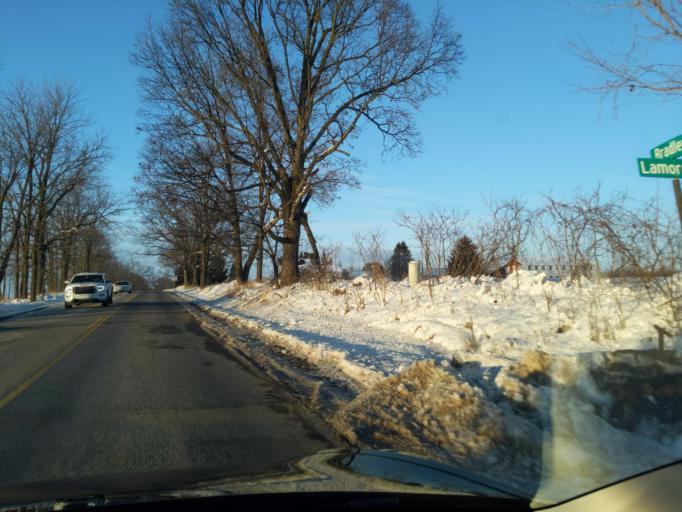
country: US
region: Michigan
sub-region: Livingston County
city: Fowlerville
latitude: 42.5571
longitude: -84.1129
